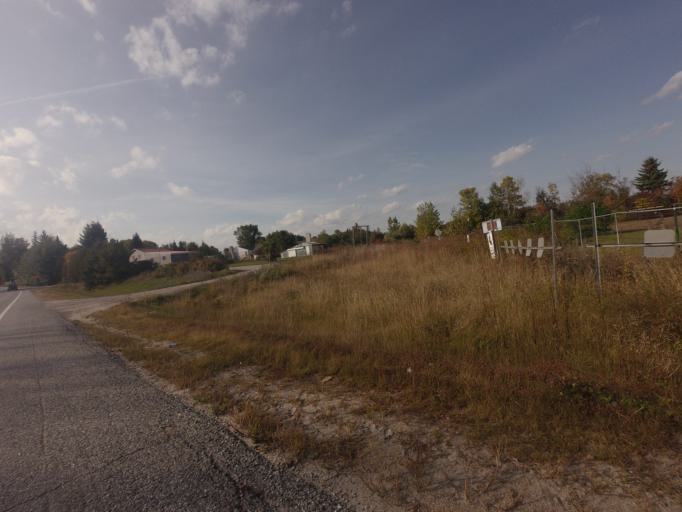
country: CA
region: Quebec
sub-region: Outaouais
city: Maniwaki
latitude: 46.3852
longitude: -75.9621
